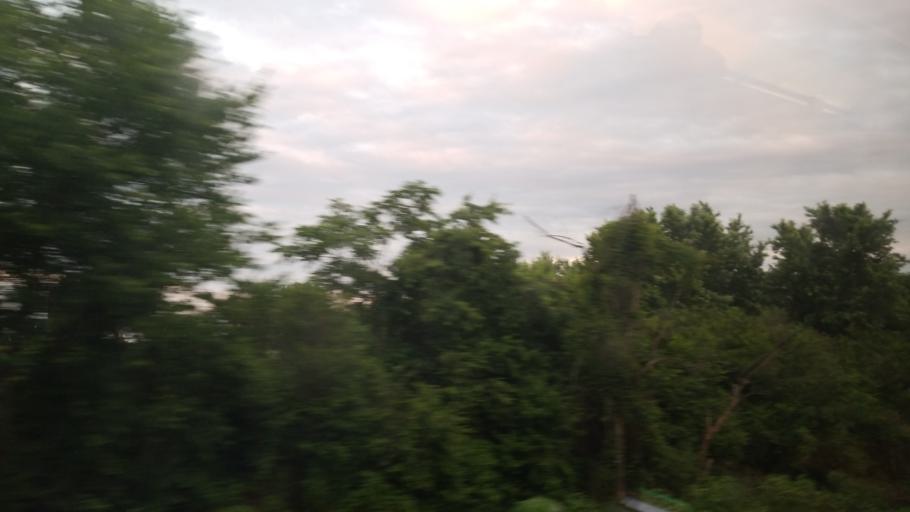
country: US
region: Virginia
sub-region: Culpeper County
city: Culpeper
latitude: 38.4293
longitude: -77.9985
